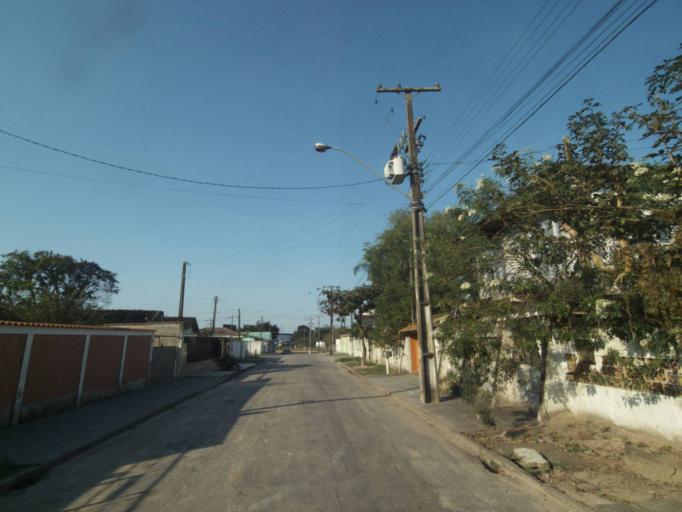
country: BR
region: Parana
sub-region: Paranagua
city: Paranagua
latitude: -25.5574
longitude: -48.5627
